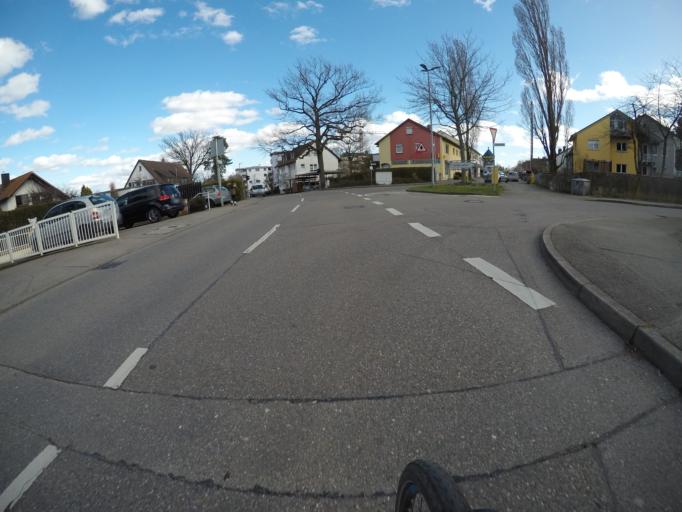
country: DE
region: Baden-Wuerttemberg
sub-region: Regierungsbezirk Stuttgart
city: Leinfelden-Echterdingen
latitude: 48.6656
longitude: 9.1733
